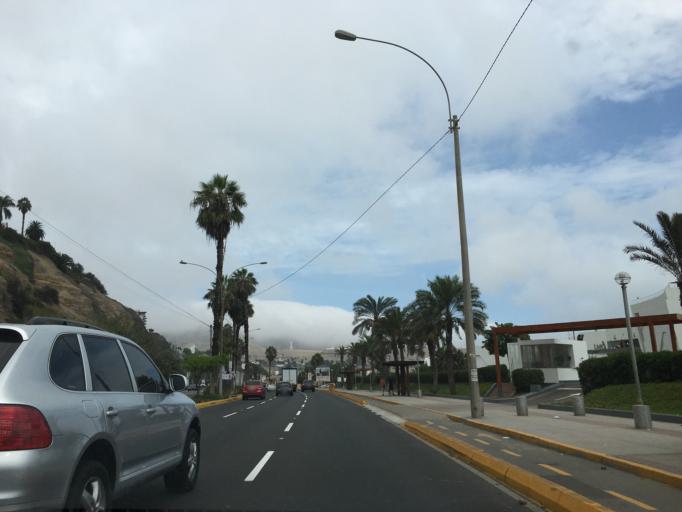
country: PE
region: Lima
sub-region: Lima
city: Surco
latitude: -12.1543
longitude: -77.0249
